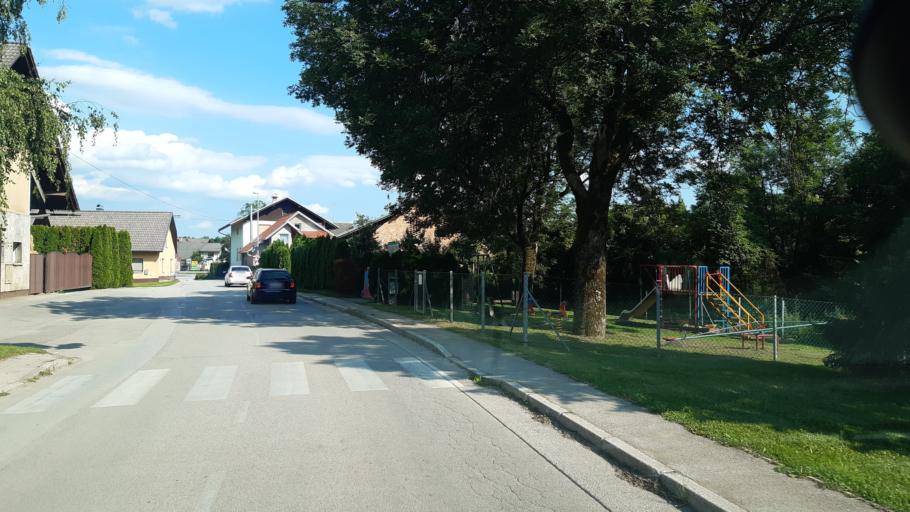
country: SI
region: Sencur
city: Hrastje
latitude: 46.2127
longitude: 14.3949
